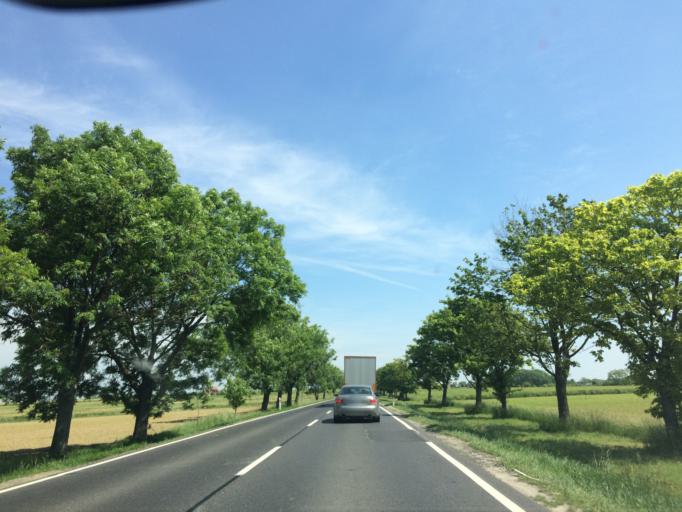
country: PL
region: Lower Silesian Voivodeship
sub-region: Powiat wroclawski
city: Gniechowice
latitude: 51.0030
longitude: 16.8543
